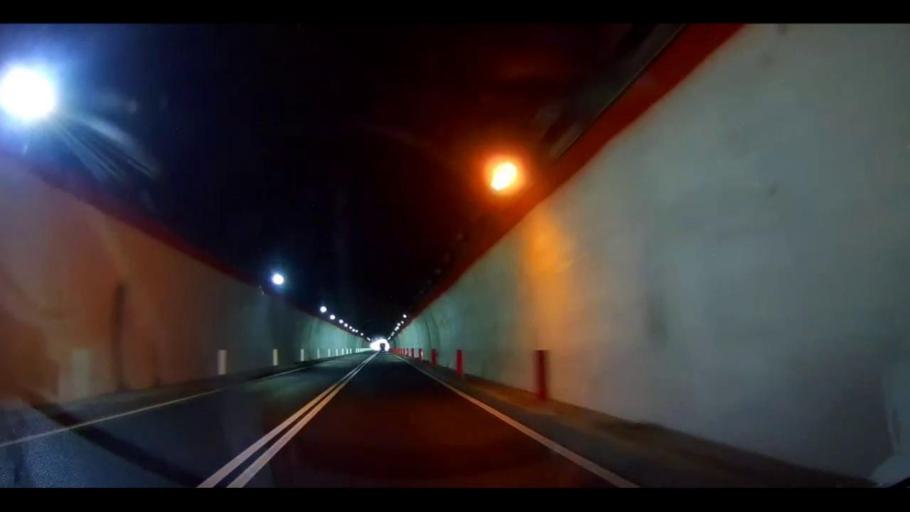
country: IT
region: Calabria
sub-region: Provincia di Cosenza
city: Spezzano della Sila
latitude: 39.3021
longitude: 16.3555
